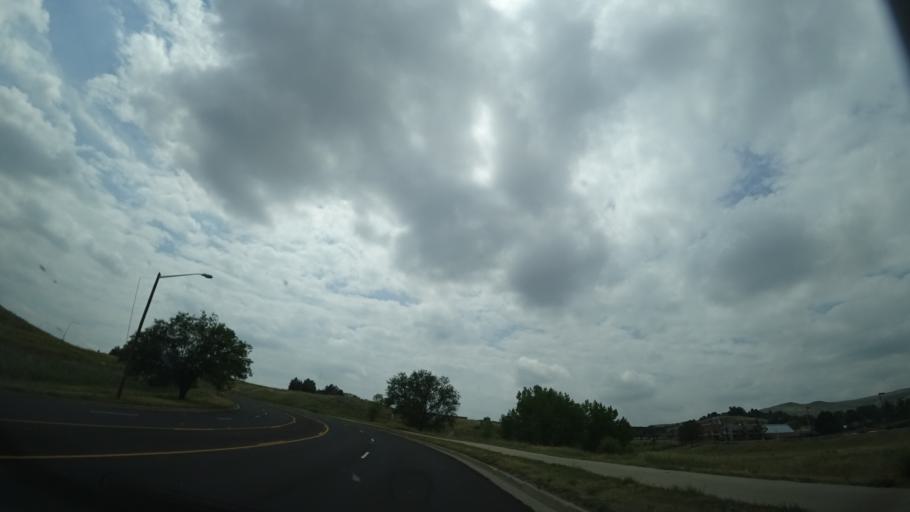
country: US
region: Colorado
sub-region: Jefferson County
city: West Pleasant View
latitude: 39.7235
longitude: -105.1514
